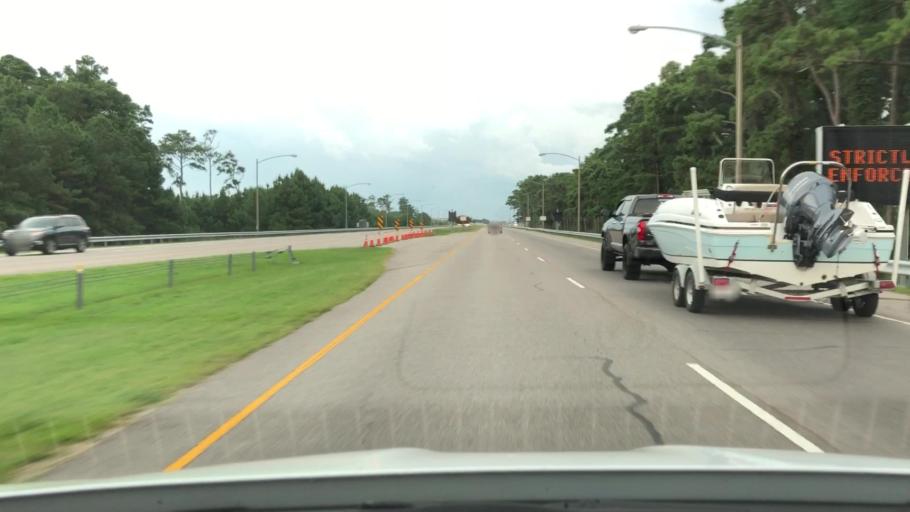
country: US
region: Virginia
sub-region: Northampton County
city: Cape Charles
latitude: 37.1286
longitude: -75.9676
